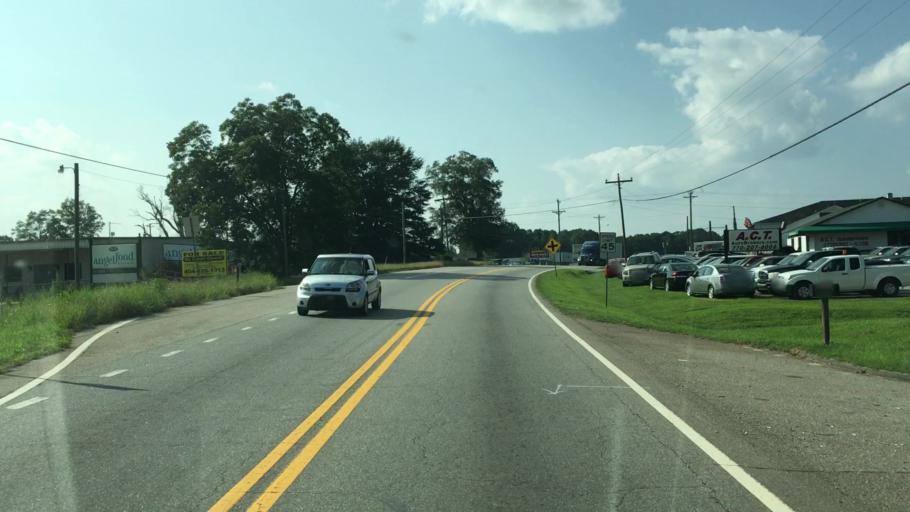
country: US
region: Georgia
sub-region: Walton County
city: Monroe
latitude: 33.7709
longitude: -83.7014
